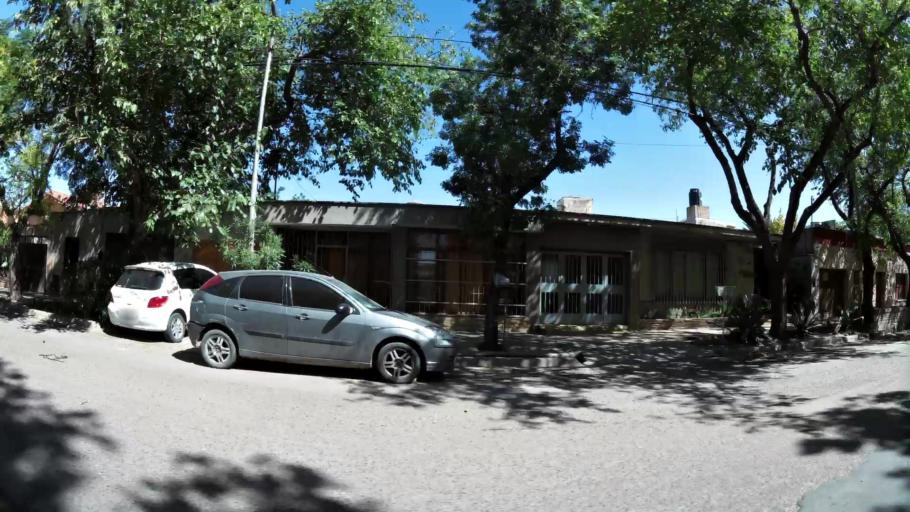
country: AR
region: Mendoza
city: Villa Nueva
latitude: -32.8950
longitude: -68.7828
